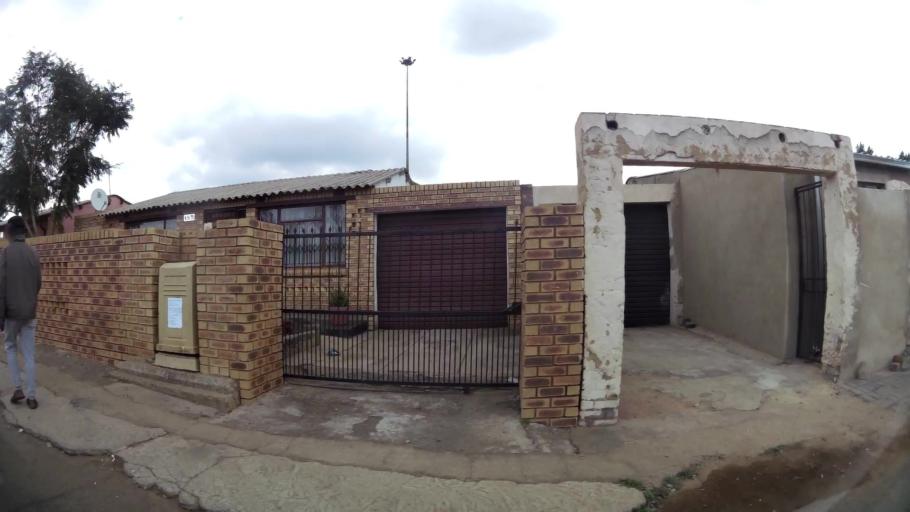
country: ZA
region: Gauteng
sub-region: City of Johannesburg Metropolitan Municipality
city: Soweto
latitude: -26.2706
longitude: 27.8711
